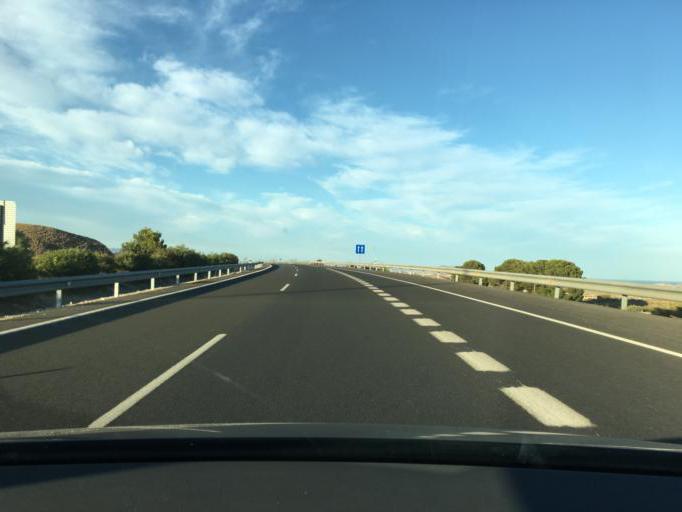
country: ES
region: Andalusia
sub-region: Provincia de Almeria
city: Bedar
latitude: 37.1613
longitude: -1.9475
